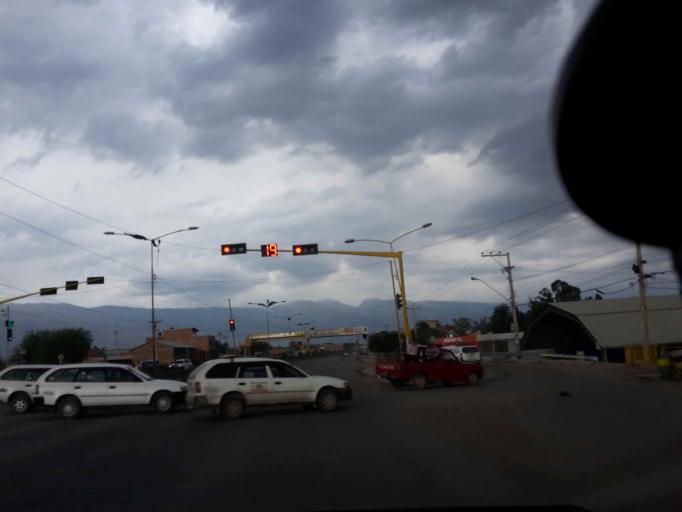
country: BO
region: Cochabamba
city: Sipe Sipe
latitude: -17.3987
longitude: -66.3266
